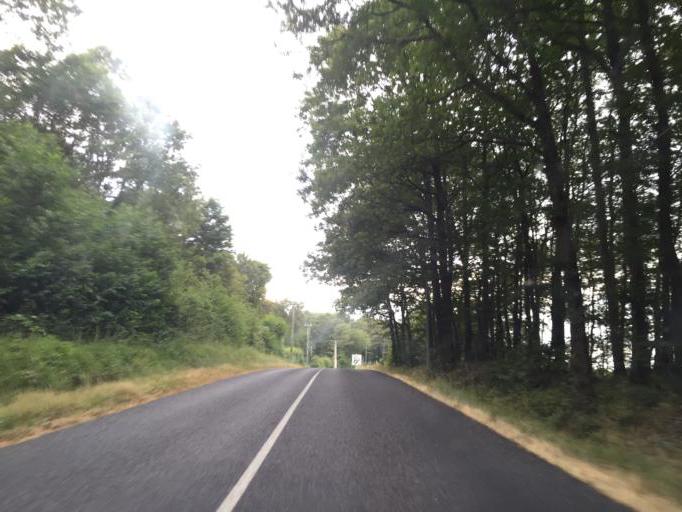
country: FR
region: Auvergne
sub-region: Departement de l'Allier
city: Lusigny
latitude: 46.5340
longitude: 3.4479
